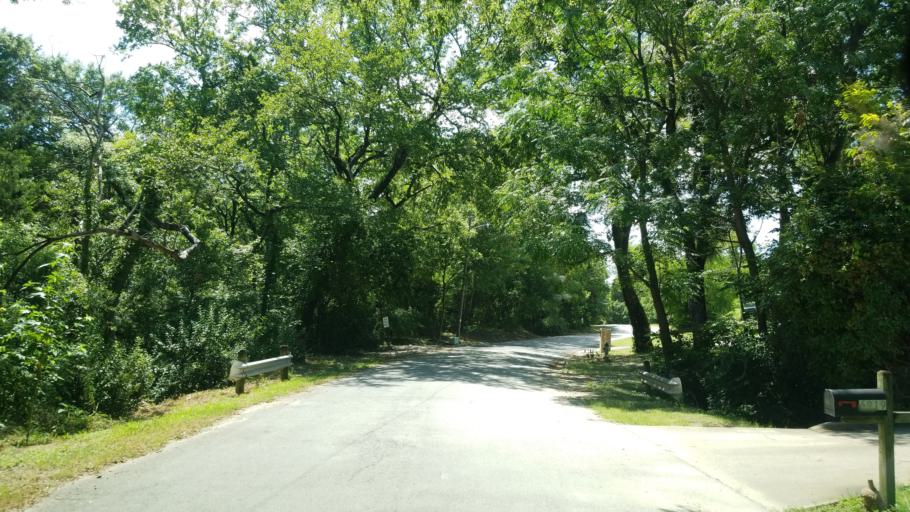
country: US
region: Texas
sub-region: Dallas County
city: Balch Springs
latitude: 32.7611
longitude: -96.7024
